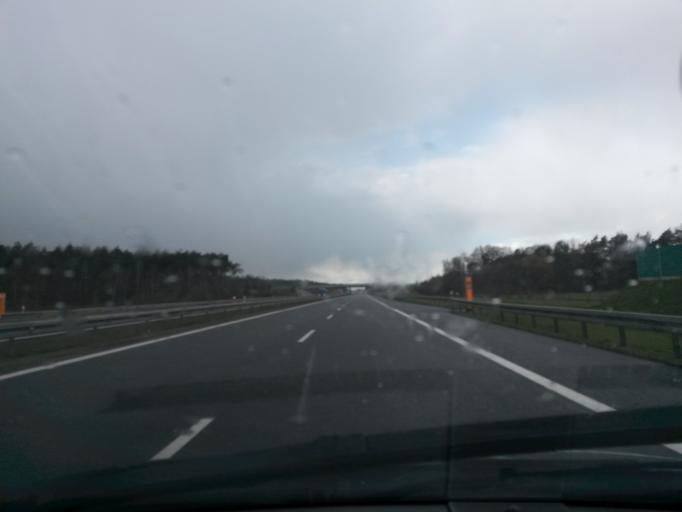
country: PL
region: Greater Poland Voivodeship
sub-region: Powiat koninski
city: Stare Miasto
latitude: 52.1734
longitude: 18.1510
